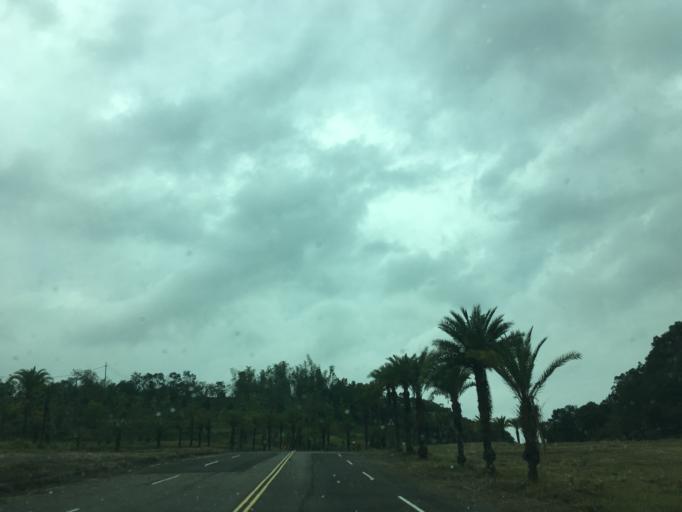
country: TW
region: Taiwan
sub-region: Taichung City
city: Taichung
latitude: 24.0601
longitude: 120.7264
